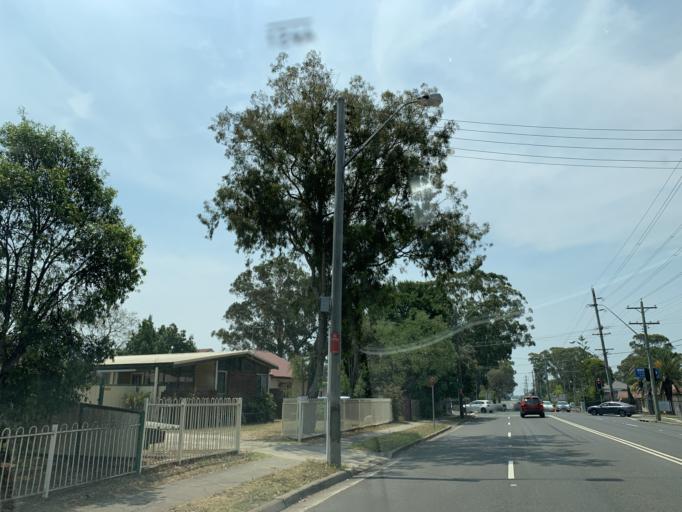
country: AU
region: New South Wales
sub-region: Blacktown
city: Blacktown
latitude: -33.7697
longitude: 150.8923
